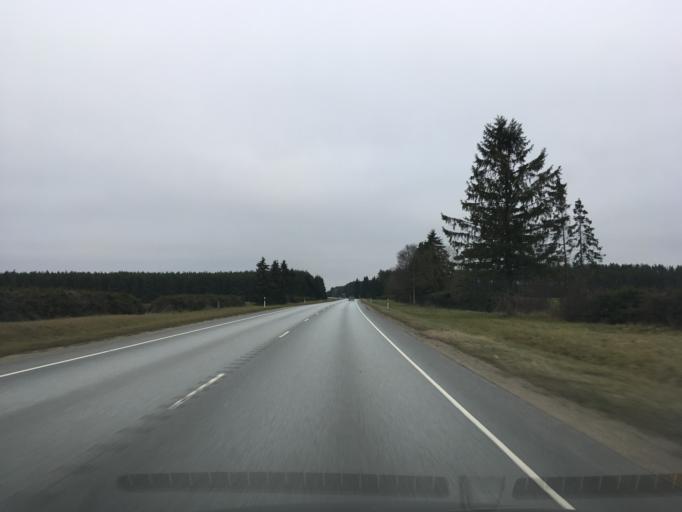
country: EE
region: Laeaene-Virumaa
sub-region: Viru-Nigula vald
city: Kunda
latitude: 59.3908
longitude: 26.6189
